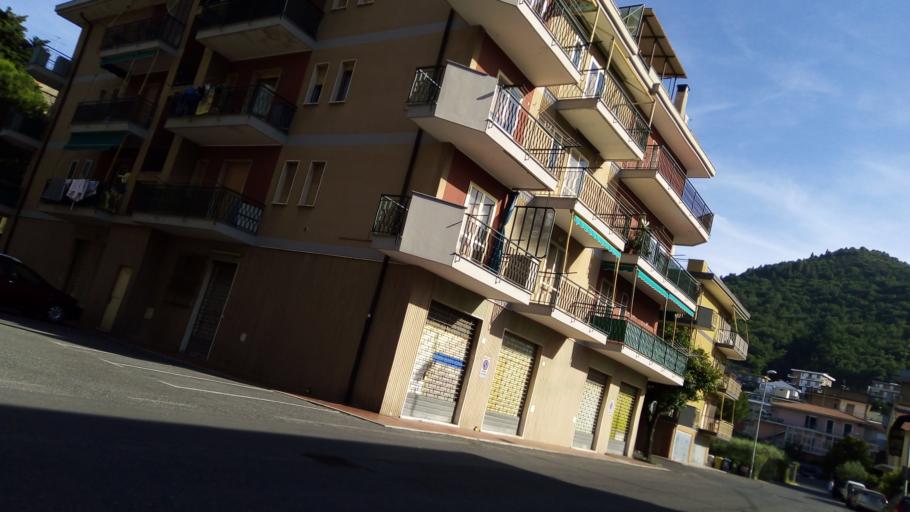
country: IT
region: Liguria
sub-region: Provincia di Savona
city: Borghetto Santo Spirito
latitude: 44.1132
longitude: 8.2384
